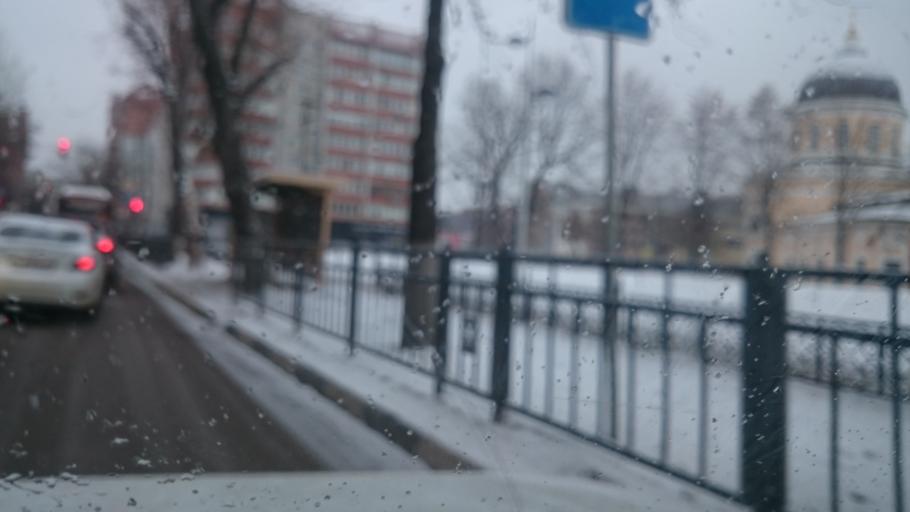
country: RU
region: Tula
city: Tula
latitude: 54.1925
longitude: 37.6067
